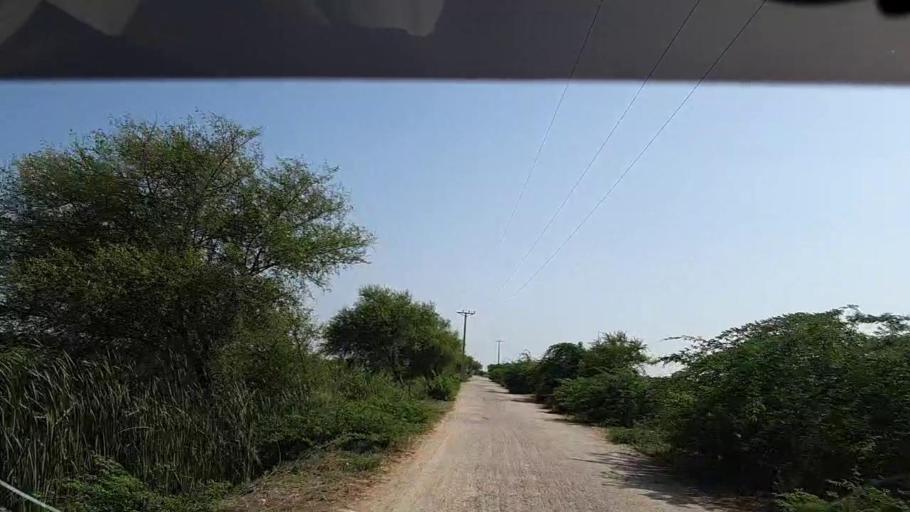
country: PK
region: Sindh
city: Badin
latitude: 24.6462
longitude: 68.7879
